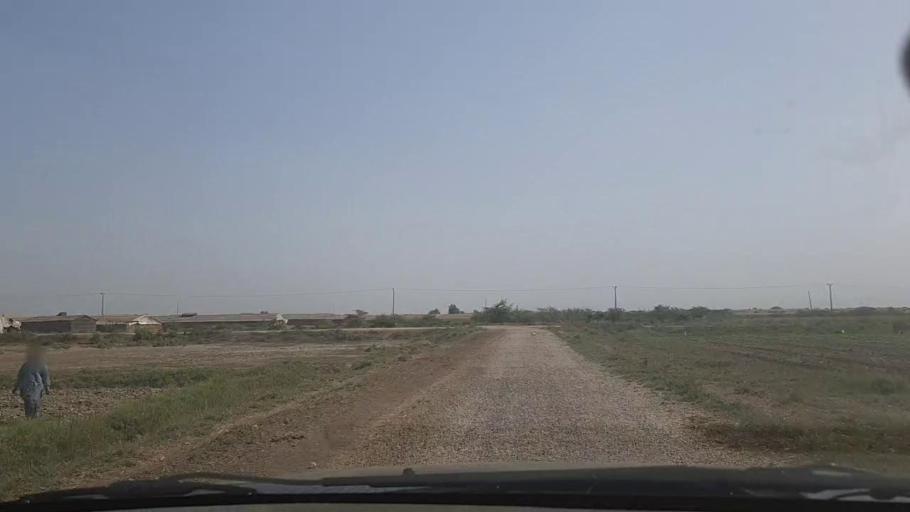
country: PK
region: Sindh
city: Keti Bandar
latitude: 24.1984
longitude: 67.5494
